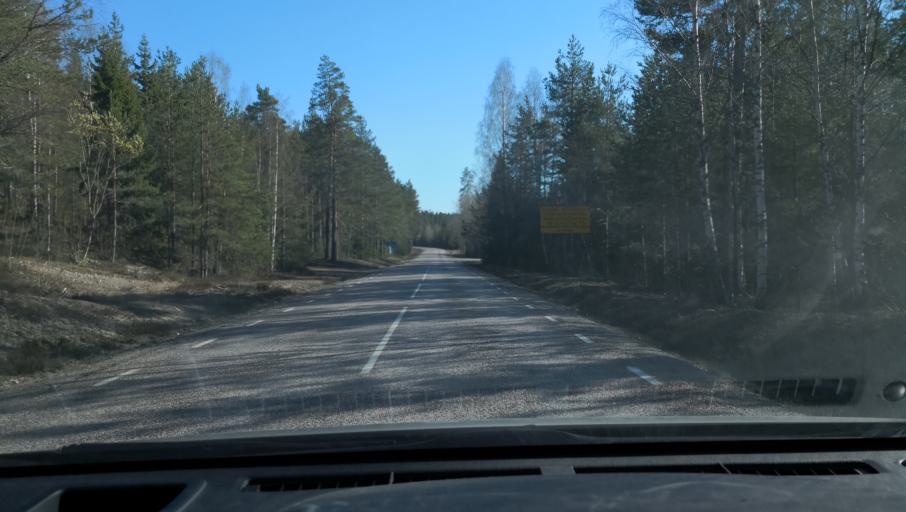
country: SE
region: Dalarna
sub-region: Avesta Kommun
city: Avesta
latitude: 60.0281
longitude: 16.3341
